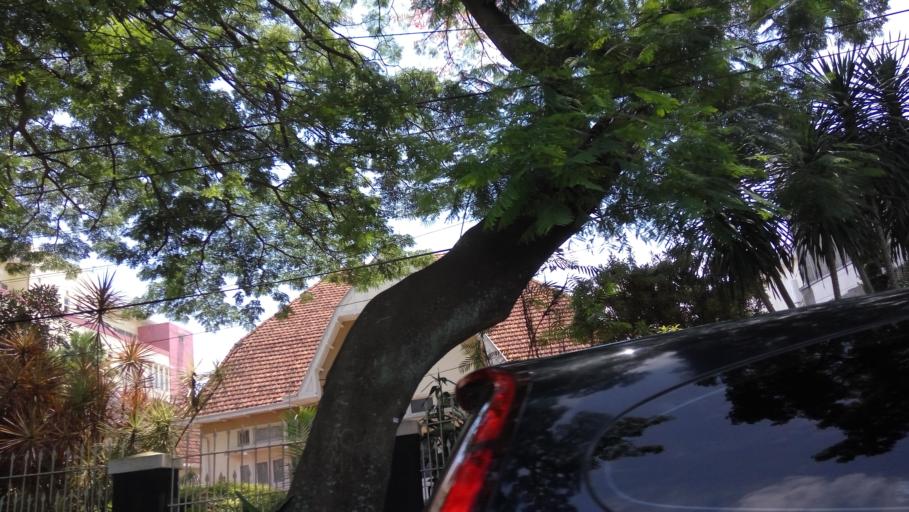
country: ID
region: East Java
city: Malang
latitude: -7.9471
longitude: 112.6403
